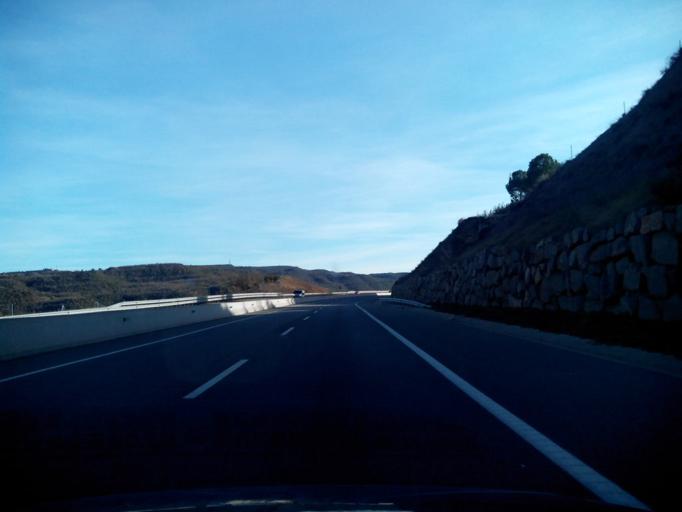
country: ES
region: Catalonia
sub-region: Provincia de Barcelona
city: Gironella
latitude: 42.0130
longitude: 1.8815
